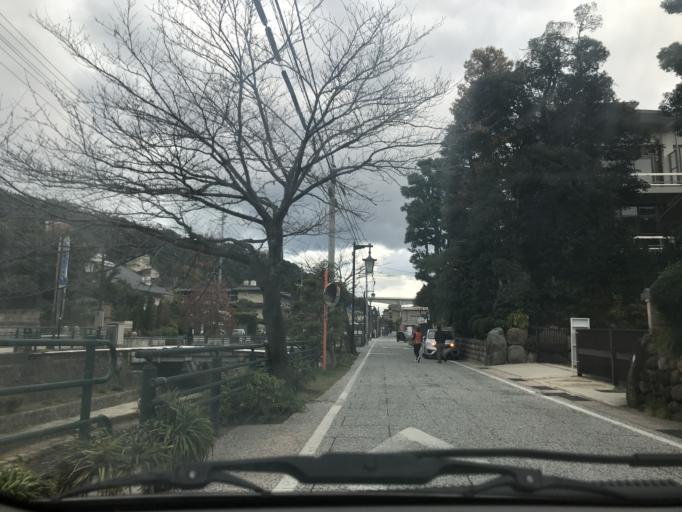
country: JP
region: Shimane
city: Matsue-shi
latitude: 35.4161
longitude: 133.0098
